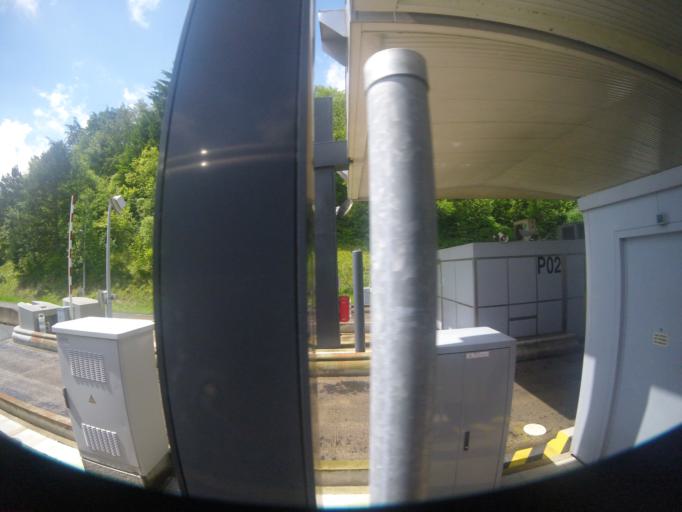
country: FR
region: Lorraine
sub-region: Departement de la Meuse
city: Dugny-sur-Meuse
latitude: 49.1109
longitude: 5.4139
